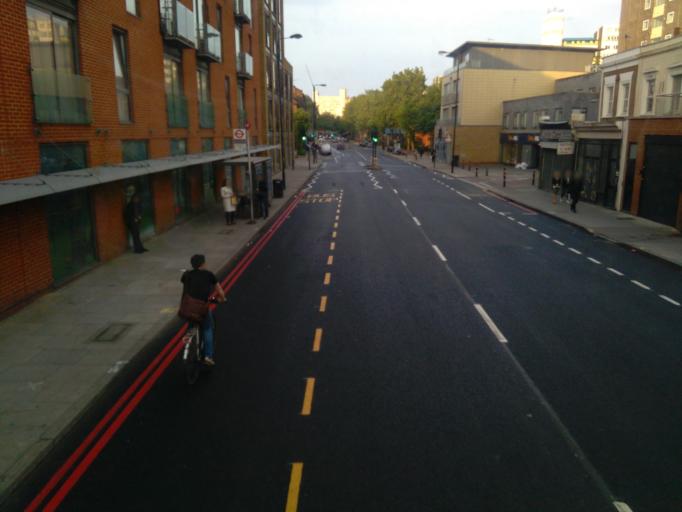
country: GB
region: England
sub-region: Greater London
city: Battersea
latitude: 51.4743
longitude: -0.1569
